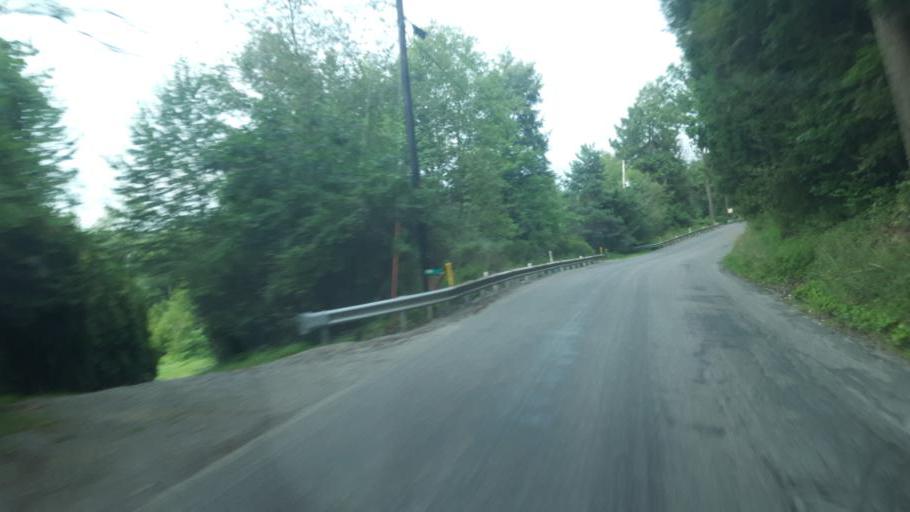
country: US
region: Pennsylvania
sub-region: Clarion County
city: Knox
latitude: 41.1611
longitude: -79.5358
